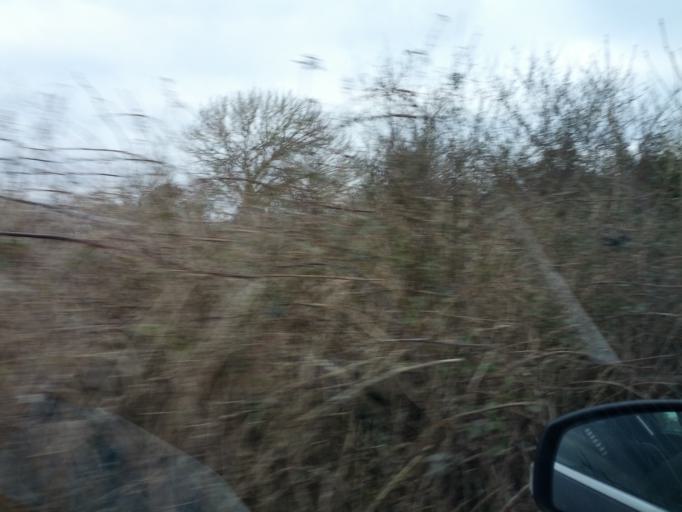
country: IE
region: Connaught
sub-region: County Galway
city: Oranmore
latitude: 53.2149
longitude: -8.8578
